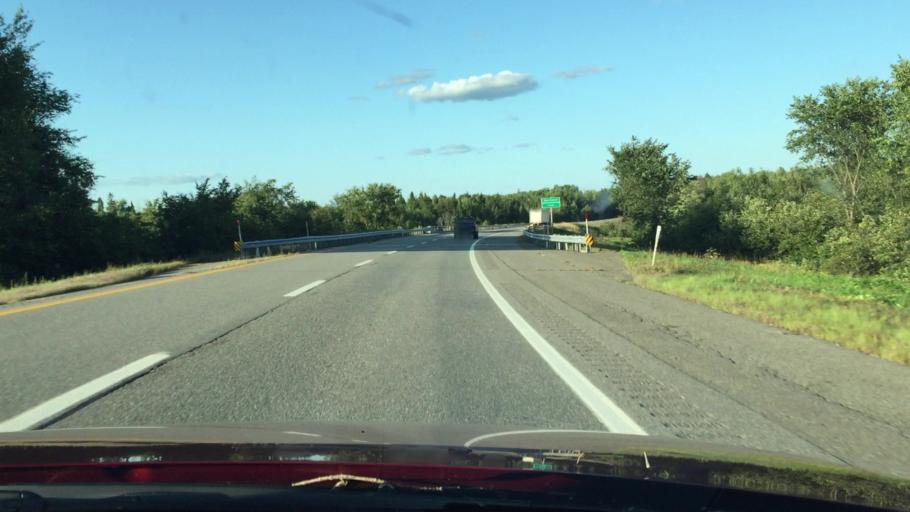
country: US
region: Maine
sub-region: Penobscot County
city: Patten
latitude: 46.0242
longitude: -68.2868
